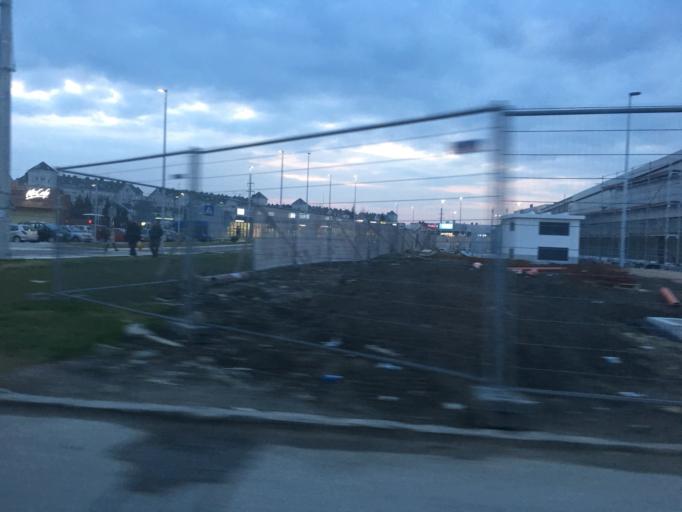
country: RS
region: Central Serbia
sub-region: Belgrade
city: Stari Grad
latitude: 44.8870
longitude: 20.4596
